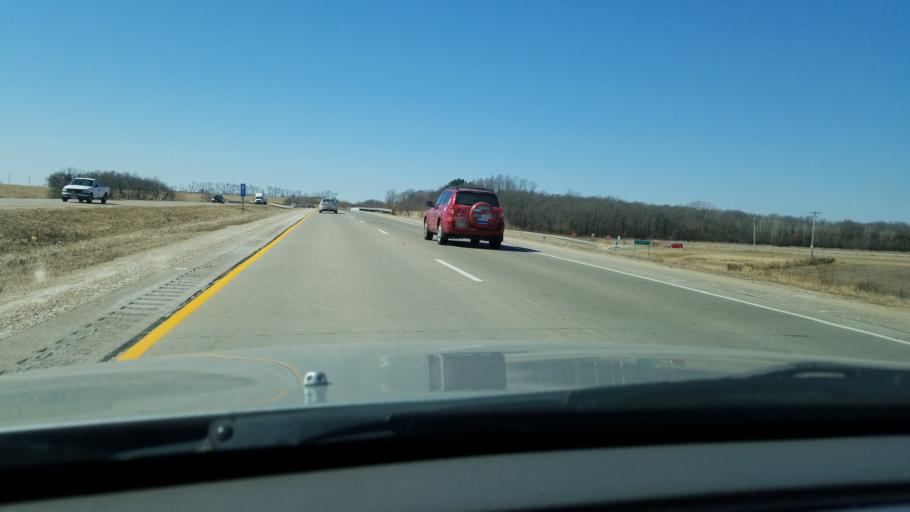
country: US
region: Wisconsin
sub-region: Dane County
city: Verona
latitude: 42.9744
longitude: -89.5431
